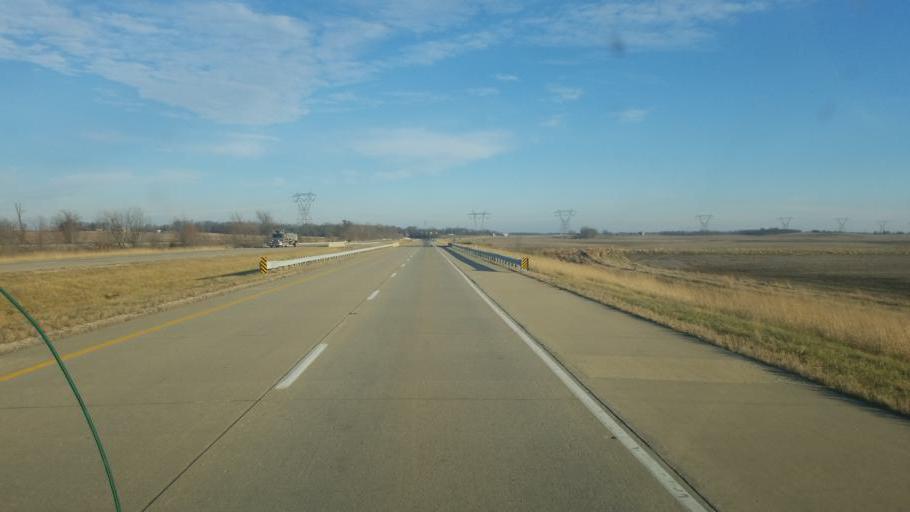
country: US
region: Indiana
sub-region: Knox County
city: Bicknell
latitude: 38.6695
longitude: -87.3413
